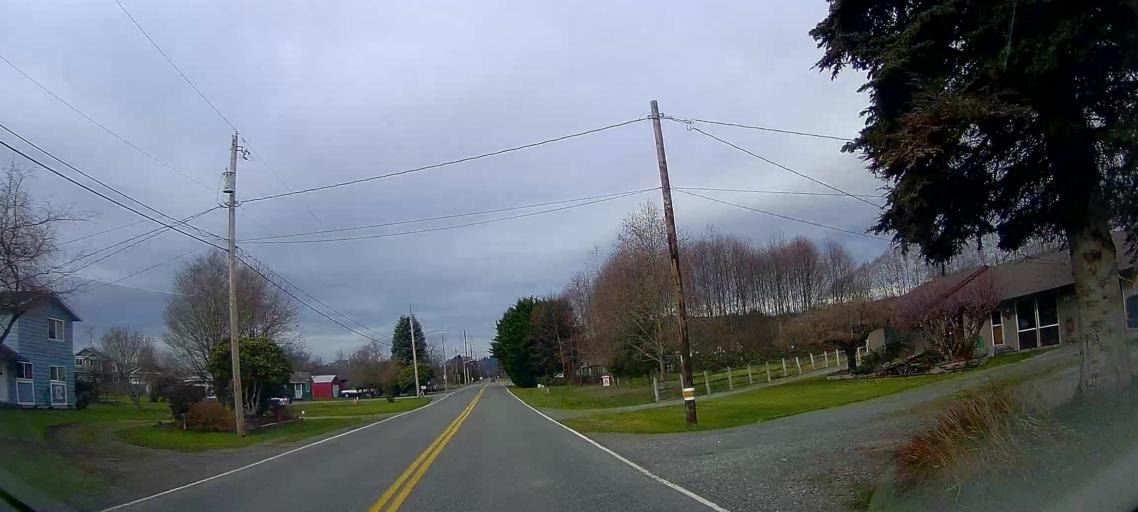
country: US
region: Washington
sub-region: Skagit County
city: Sedro-Woolley
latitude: 48.5133
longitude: -122.2522
